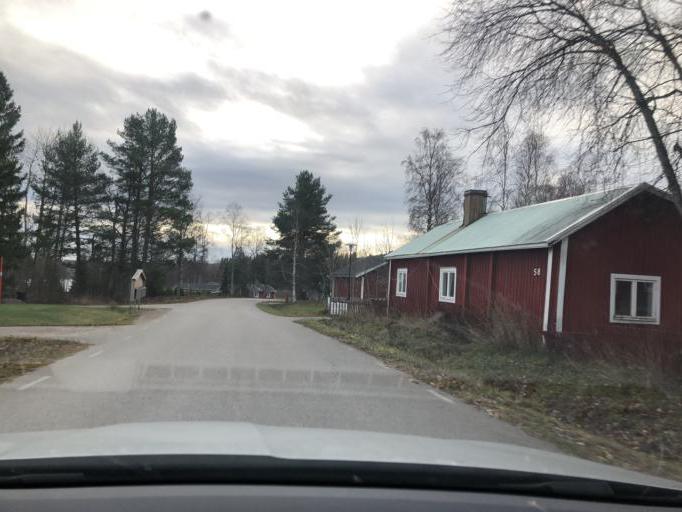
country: SE
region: Gaevleborg
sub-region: Hudiksvalls Kommun
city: Sorforsa
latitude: 61.6758
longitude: 16.9240
